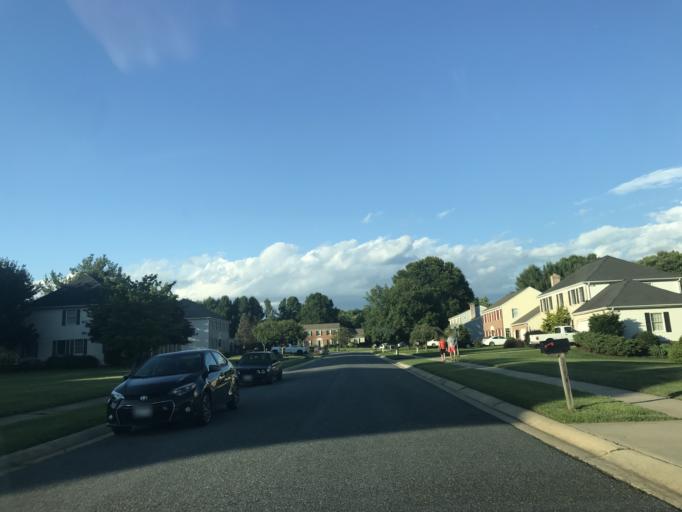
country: US
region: Maryland
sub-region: Harford County
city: South Bel Air
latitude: 39.5564
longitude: -76.3240
